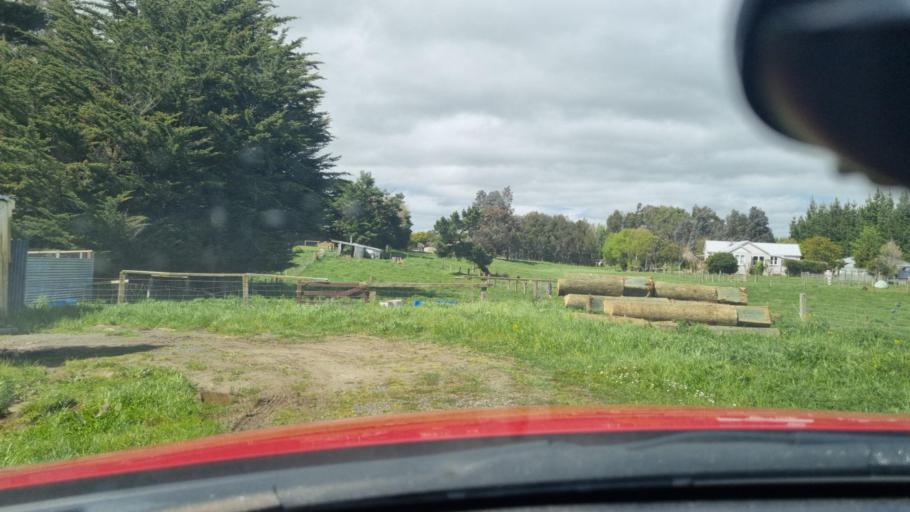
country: NZ
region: Southland
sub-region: Invercargill City
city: Invercargill
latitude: -46.3947
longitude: 168.4499
